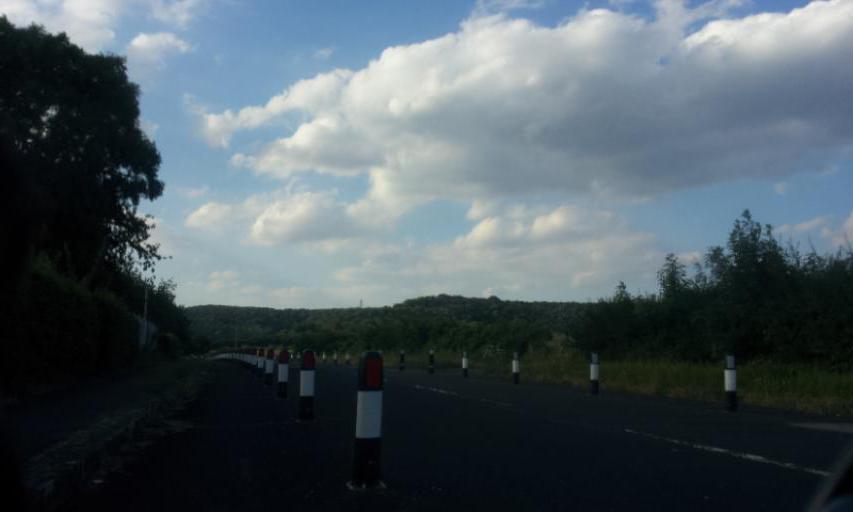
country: GB
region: England
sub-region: Kent
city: Boxley
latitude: 51.3068
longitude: 0.5143
